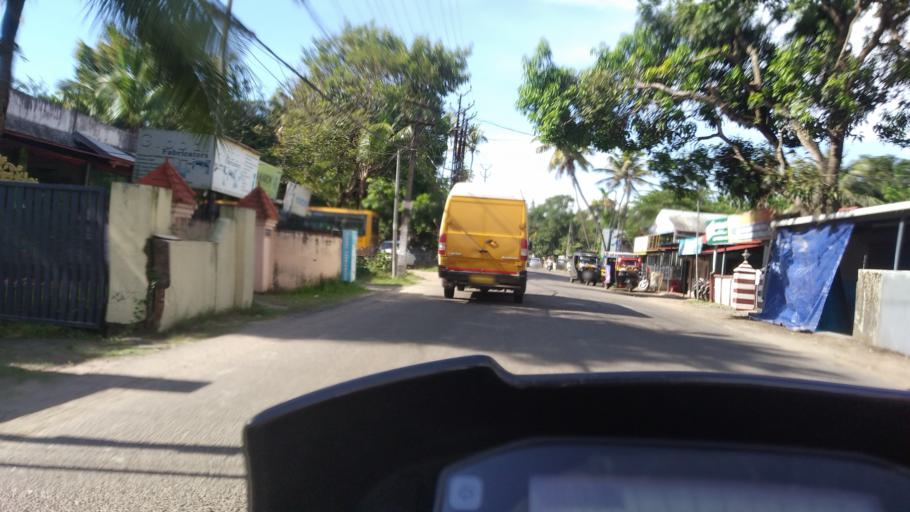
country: IN
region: Kerala
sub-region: Ernakulam
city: Elur
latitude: 10.0341
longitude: 76.2210
